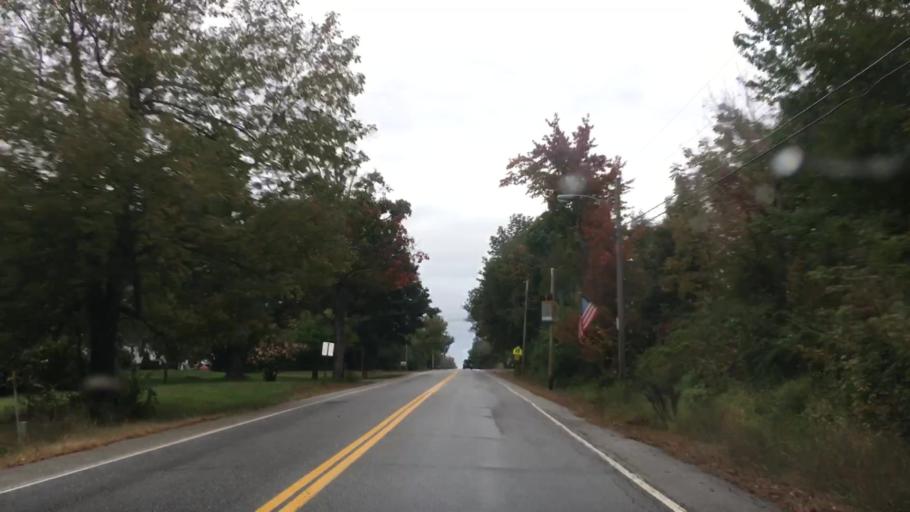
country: US
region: Maine
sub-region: Cumberland County
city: Raymond
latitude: 43.9356
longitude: -70.4432
